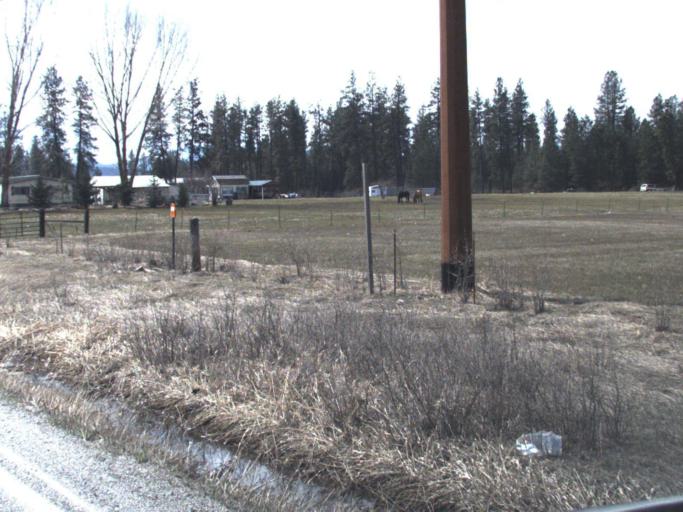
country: US
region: Washington
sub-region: Pend Oreille County
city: Newport
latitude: 48.3444
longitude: -117.3045
